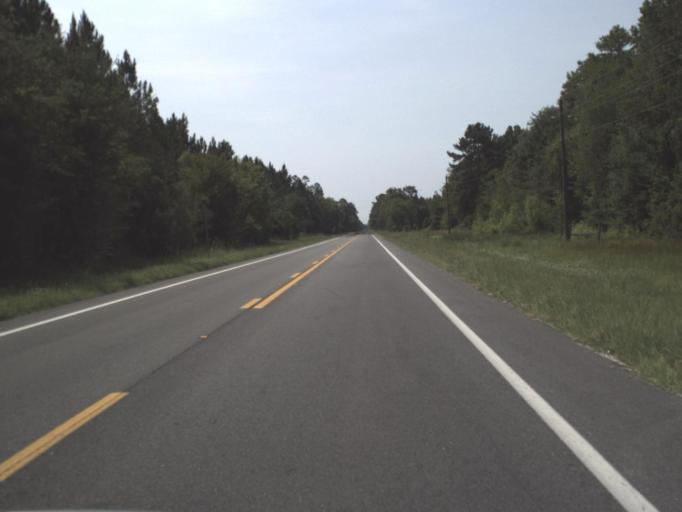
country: US
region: Florida
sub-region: Hamilton County
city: Jasper
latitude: 30.5986
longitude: -83.0125
